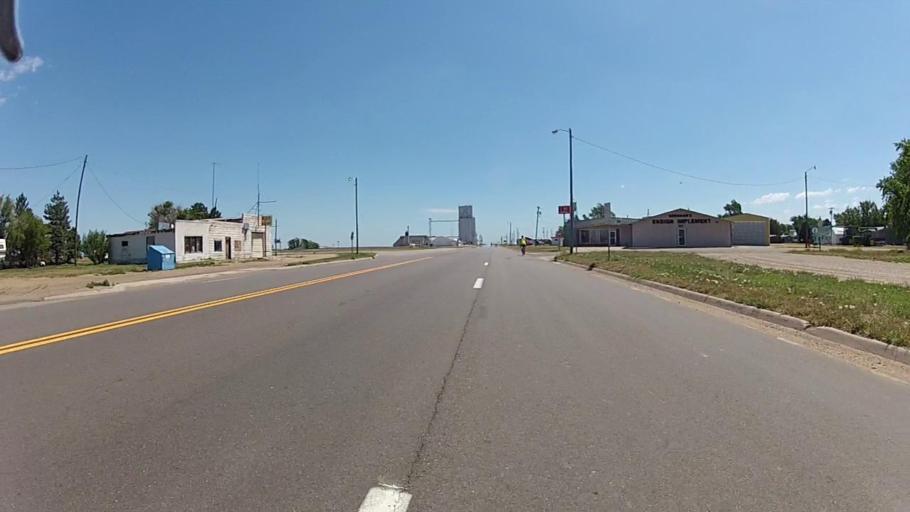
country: US
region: Kansas
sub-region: Gray County
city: Cimarron
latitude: 37.6533
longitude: -100.2339
